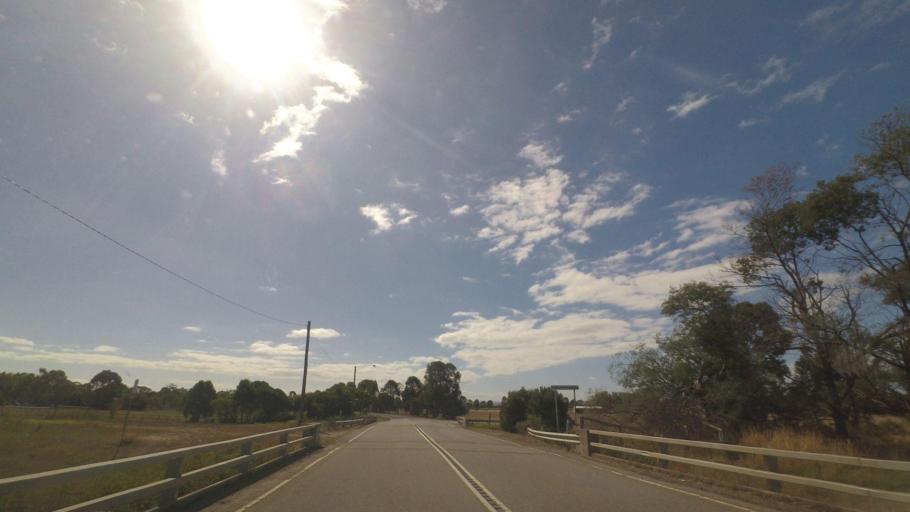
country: AU
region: Victoria
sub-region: Cardinia
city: Pakenham South
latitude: -38.1616
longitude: 145.5346
